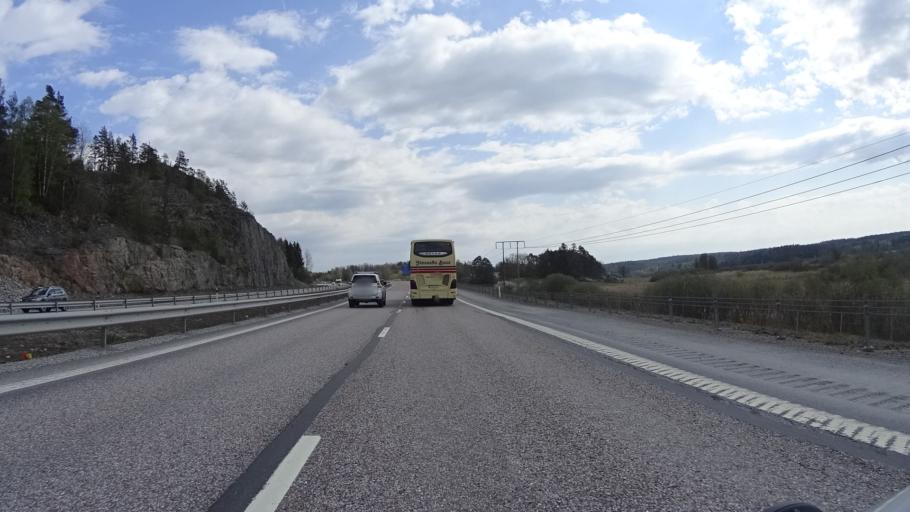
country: SE
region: Soedermanland
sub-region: Strangnas Kommun
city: Akers Styckebruk
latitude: 59.2553
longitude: 17.1501
